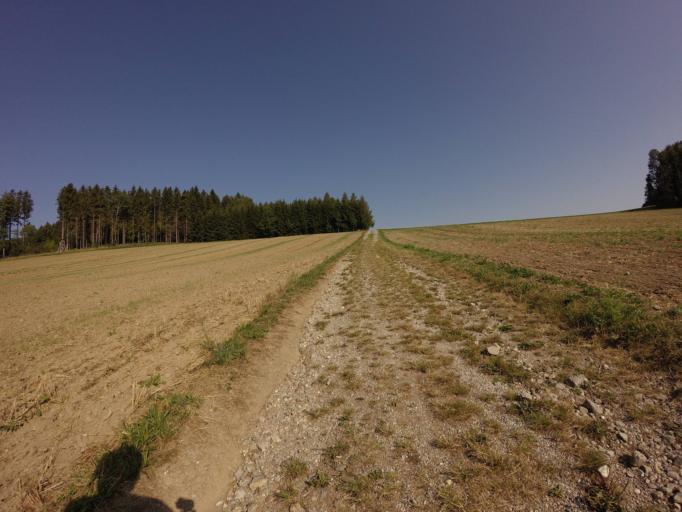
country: AT
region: Upper Austria
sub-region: Politischer Bezirk Urfahr-Umgebung
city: Bad Leonfelden
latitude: 48.5500
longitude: 14.3225
